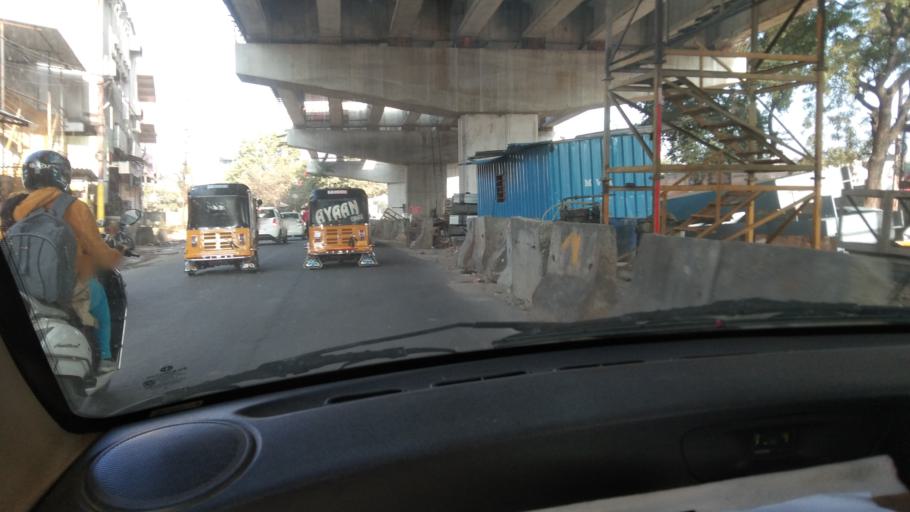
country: IN
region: Telangana
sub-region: Hyderabad
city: Hyderabad
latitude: 17.4114
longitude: 78.3964
